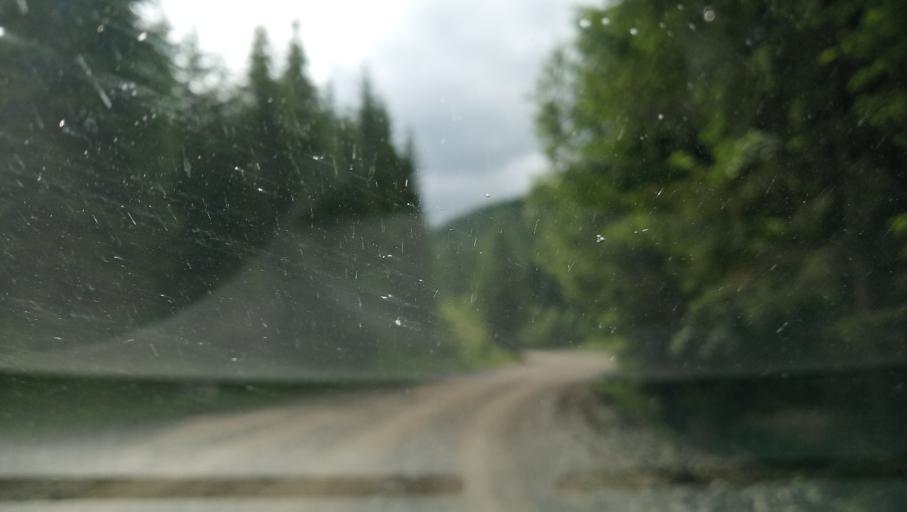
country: RO
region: Hunedoara
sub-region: Oras Petrila
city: Petrila
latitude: 45.4022
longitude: 23.5679
